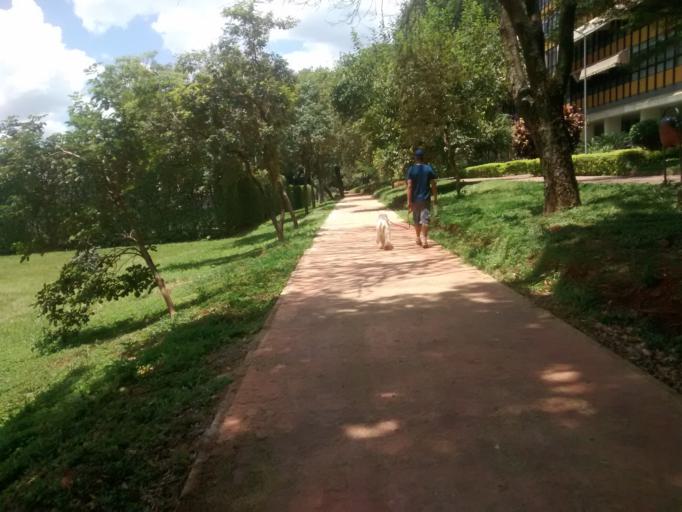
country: BR
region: Federal District
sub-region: Brasilia
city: Brasilia
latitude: -15.7662
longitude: -47.8882
